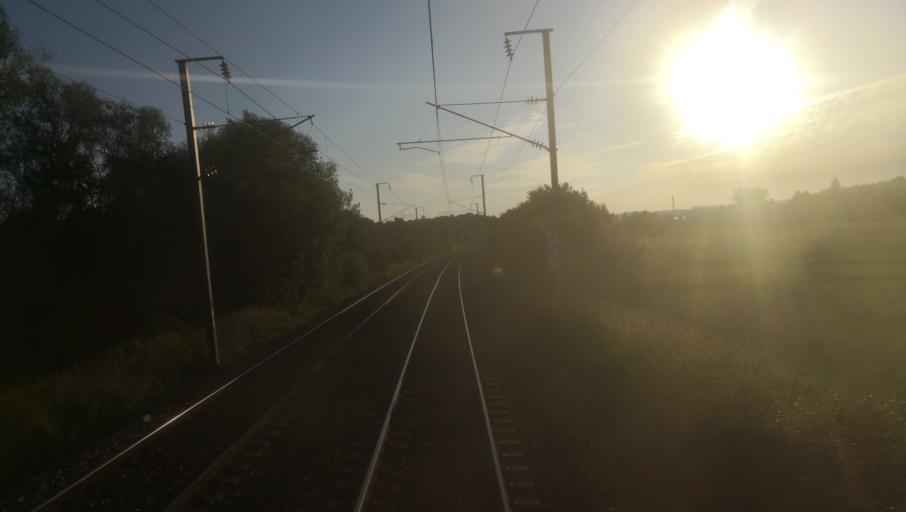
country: FR
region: Lower Normandy
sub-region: Departement du Calvados
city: Beuvillers
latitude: 49.1258
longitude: 0.2708
